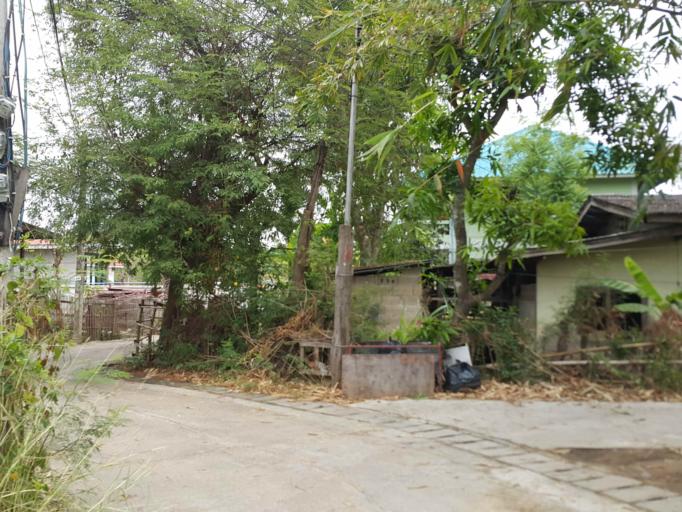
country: TH
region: Chiang Mai
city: Saraphi
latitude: 18.7542
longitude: 99.0207
